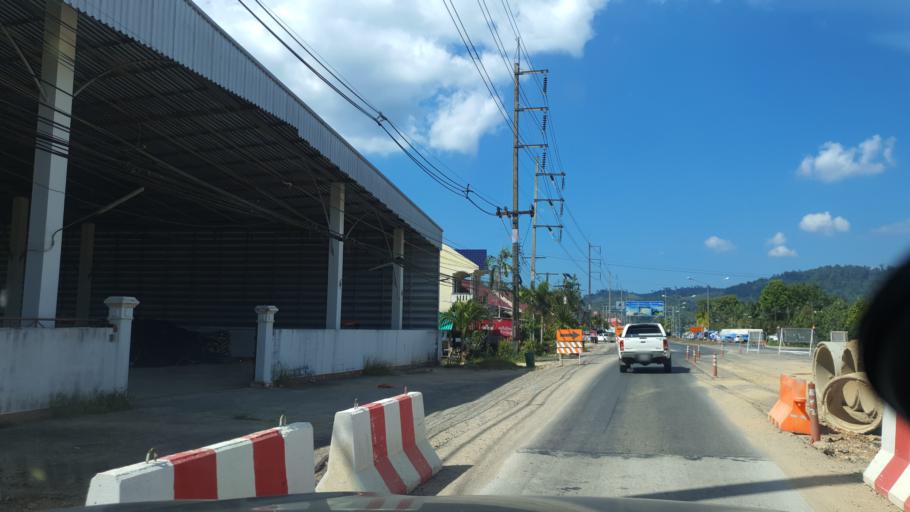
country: TH
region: Phangnga
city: Ban Khao Lak
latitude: 8.5868
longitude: 98.2586
